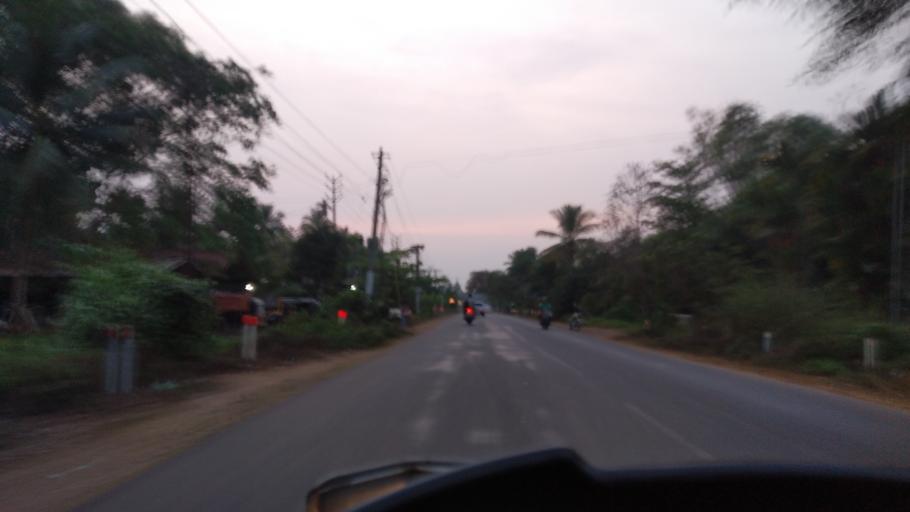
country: IN
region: Kerala
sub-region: Kottayam
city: Kottayam
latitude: 9.5921
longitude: 76.4452
